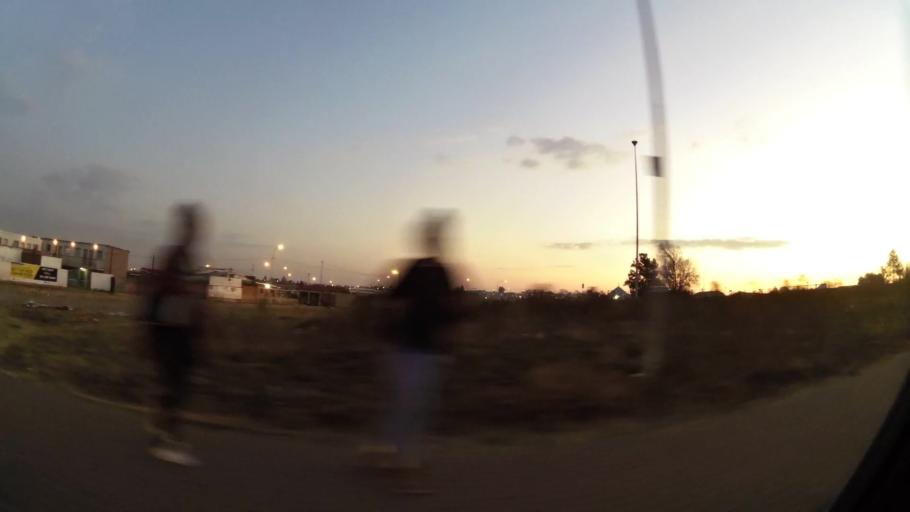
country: ZA
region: Gauteng
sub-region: City of Johannesburg Metropolitan Municipality
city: Soweto
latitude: -26.2268
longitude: 27.9107
